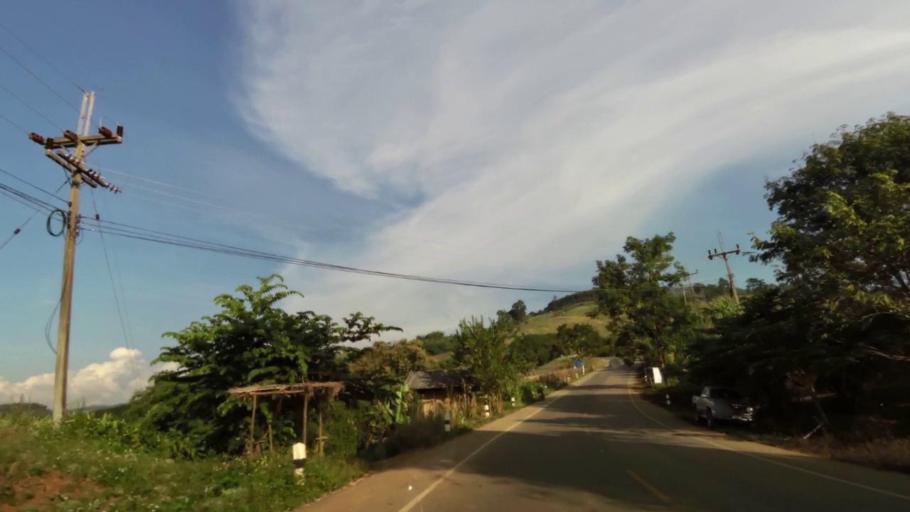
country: TH
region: Chiang Rai
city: Khun Tan
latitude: 19.8668
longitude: 100.4142
